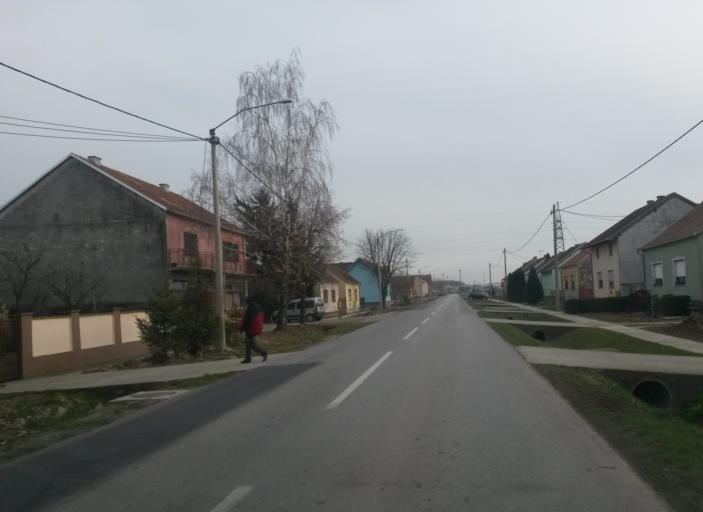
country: HR
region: Osjecko-Baranjska
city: Antunovac
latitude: 45.4774
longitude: 18.6548
